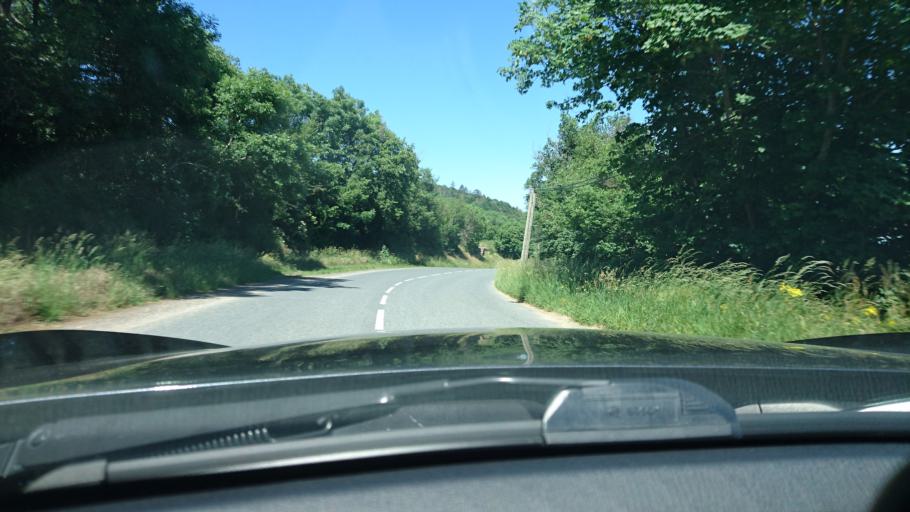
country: FR
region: Rhone-Alpes
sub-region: Departement du Rhone
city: Vaugneray
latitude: 45.7231
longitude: 4.6357
